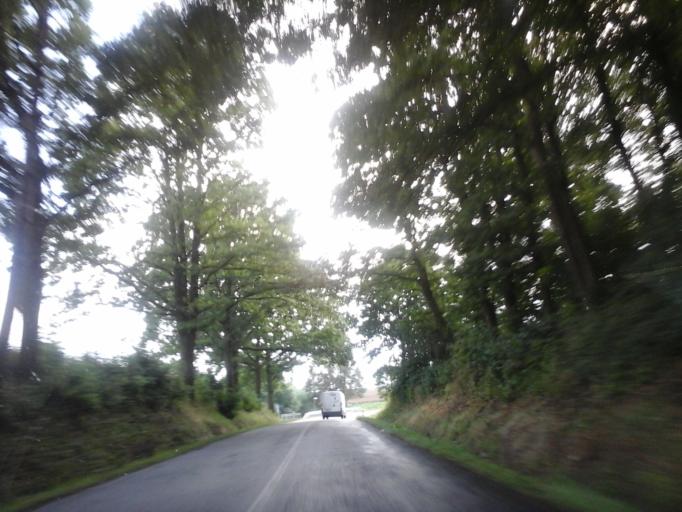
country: CZ
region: Pardubicky
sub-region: Okres Usti nad Orlici
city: Lanskroun
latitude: 49.9205
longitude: 16.6397
